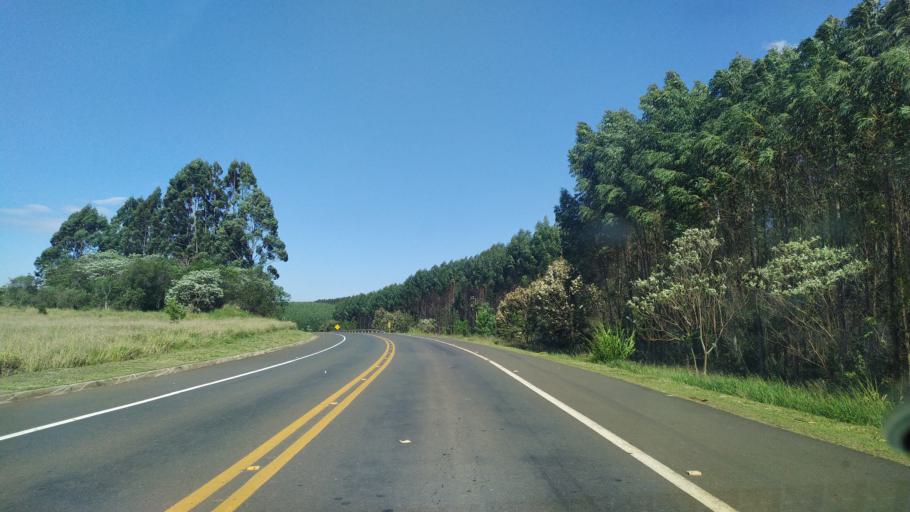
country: BR
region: Parana
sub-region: Ortigueira
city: Ortigueira
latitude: -24.2499
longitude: -50.7771
